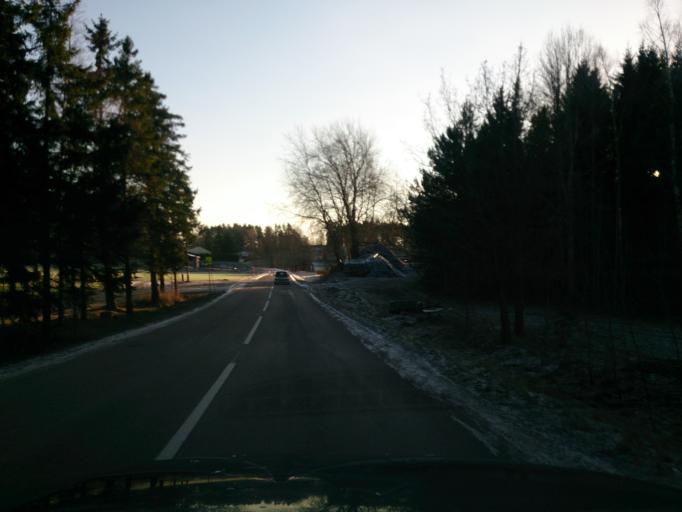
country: SE
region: OEstergoetland
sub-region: Norrkopings Kommun
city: Kimstad
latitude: 58.4192
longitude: 15.9147
